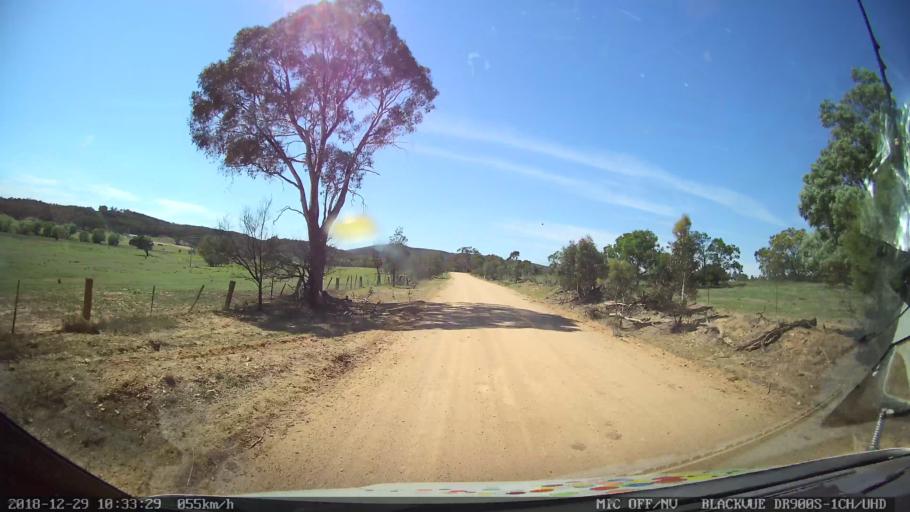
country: AU
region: New South Wales
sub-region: Yass Valley
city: Gundaroo
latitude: -34.9809
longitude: 149.4721
